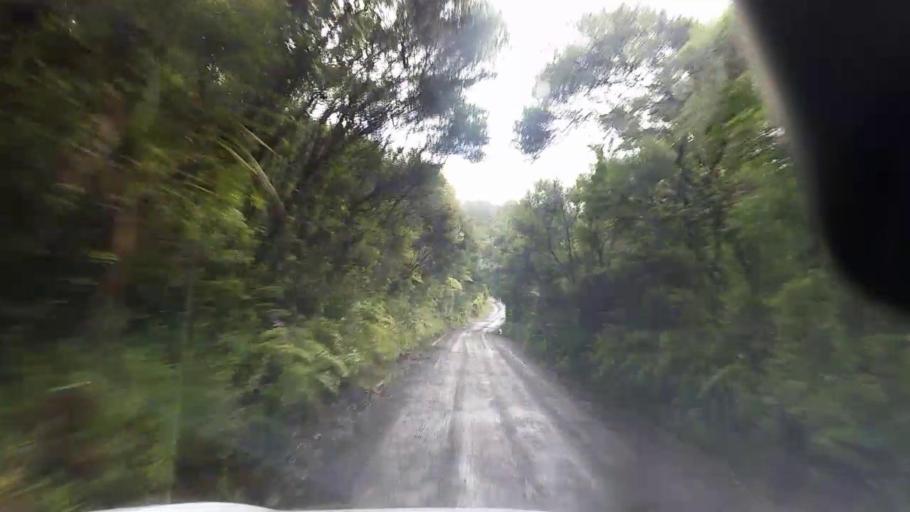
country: NZ
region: Auckland
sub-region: Auckland
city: Muriwai Beach
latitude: -36.9289
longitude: 174.5023
